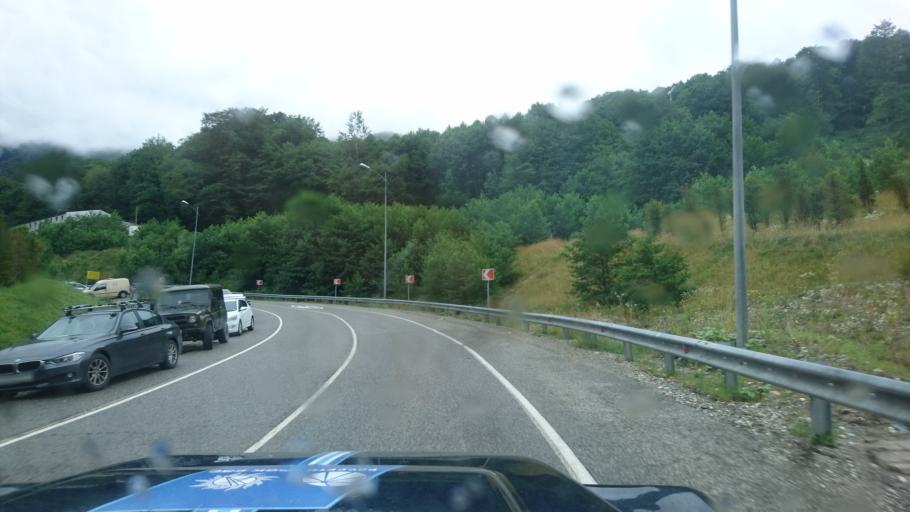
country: RU
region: Krasnodarskiy
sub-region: Sochi City
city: Krasnaya Polyana
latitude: 43.6745
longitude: 40.2841
